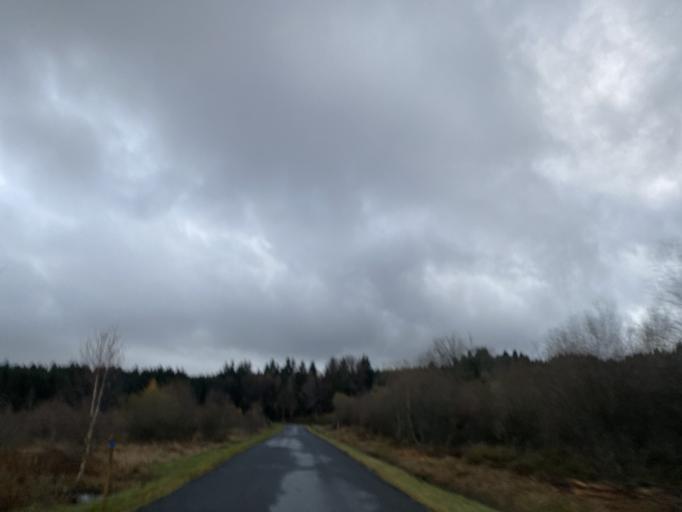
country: FR
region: Auvergne
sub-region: Departement du Puy-de-Dome
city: Cunlhat
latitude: 45.5578
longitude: 3.5733
